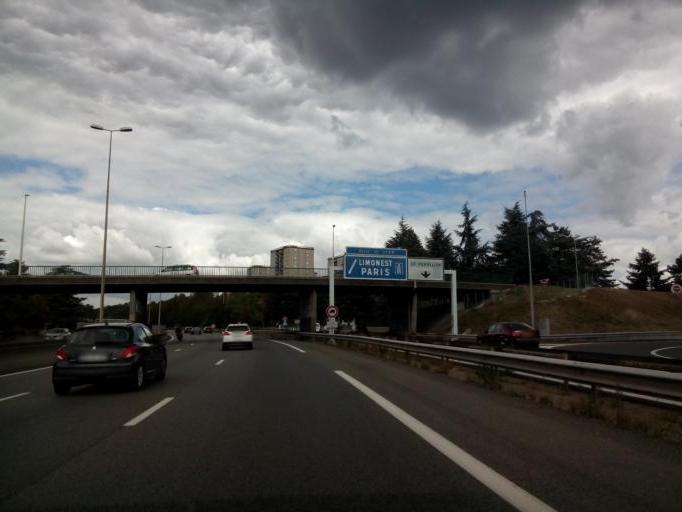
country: FR
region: Rhone-Alpes
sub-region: Departement du Rhone
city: Ecully
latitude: 45.7863
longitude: 4.7850
